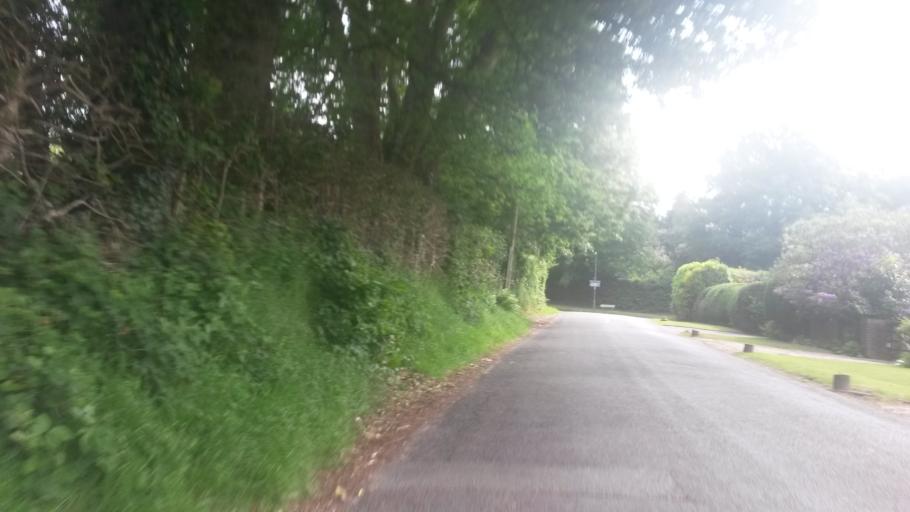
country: GB
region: England
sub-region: Surrey
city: Haslemere
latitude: 51.0825
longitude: -0.7102
